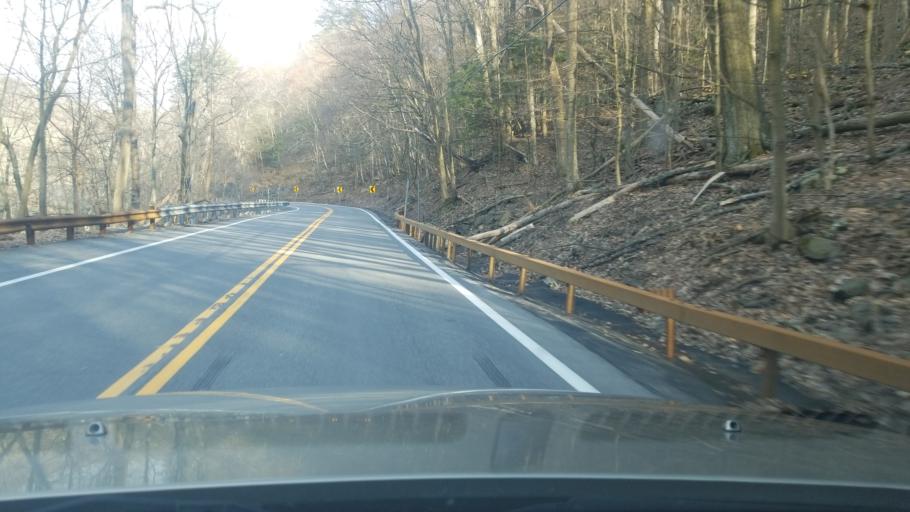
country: US
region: New York
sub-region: Greene County
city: Palenville
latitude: 42.1762
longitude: -74.0415
